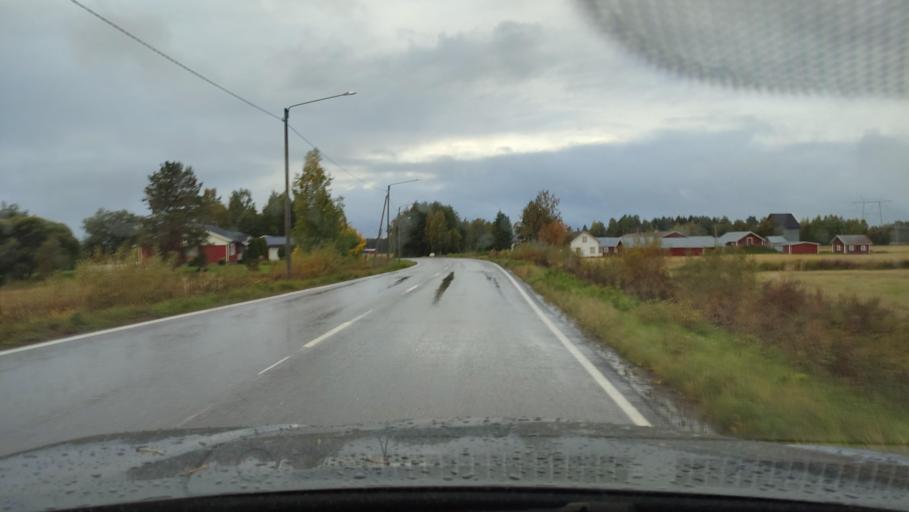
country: FI
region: Southern Ostrobothnia
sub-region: Suupohja
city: Karijoki
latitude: 62.2345
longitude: 21.6171
